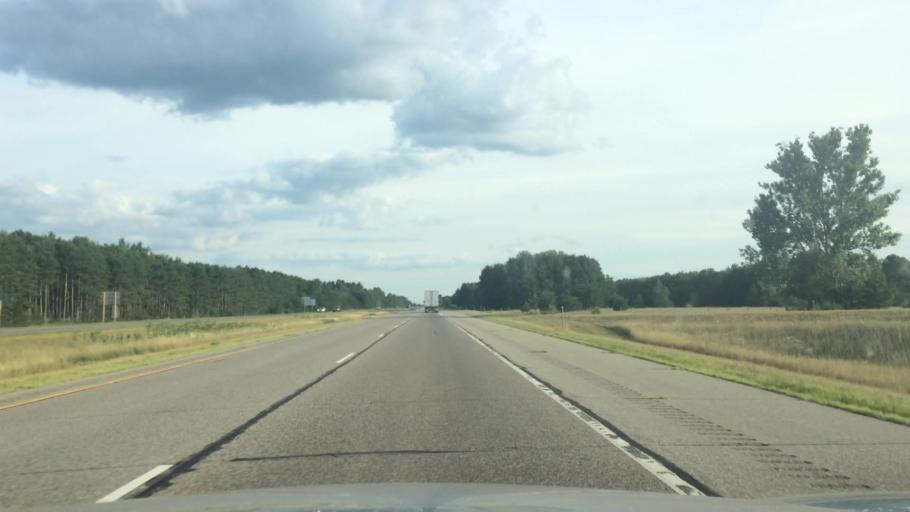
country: US
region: Wisconsin
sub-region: Portage County
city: Plover
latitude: 44.2575
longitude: -89.5241
